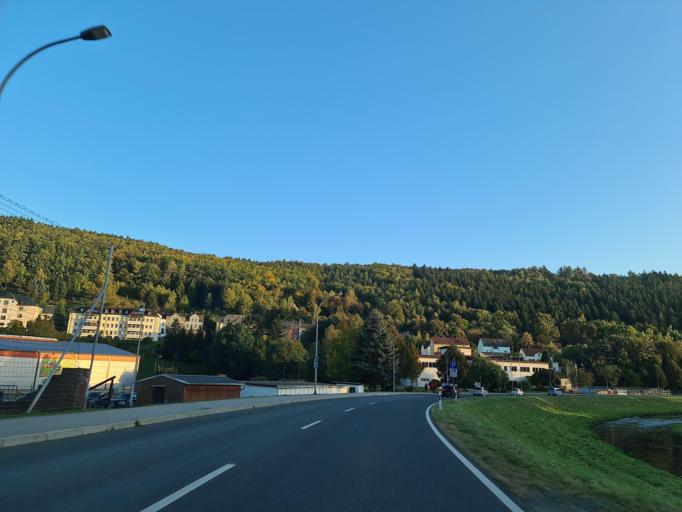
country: DE
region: Saxony
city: Elsterberg
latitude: 50.6102
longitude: 12.1747
